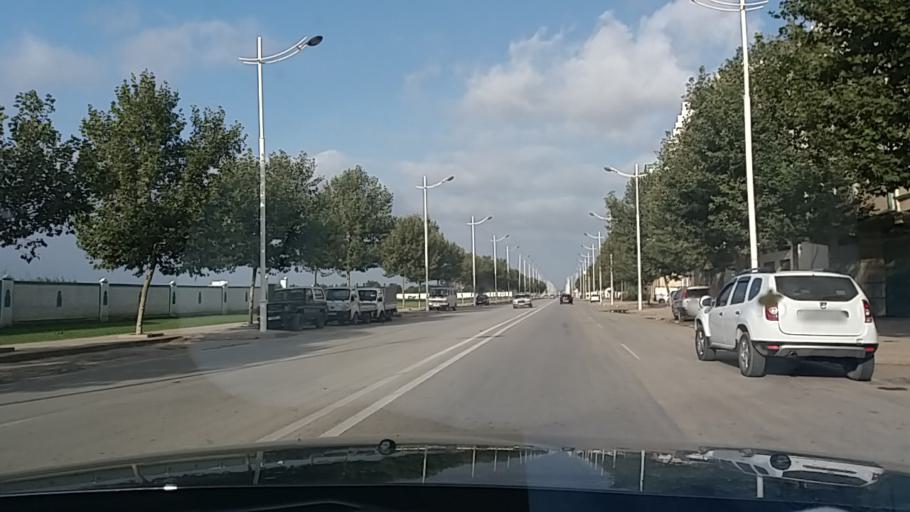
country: MA
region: Tanger-Tetouan
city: Tetouan
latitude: 35.5661
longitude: -5.3419
